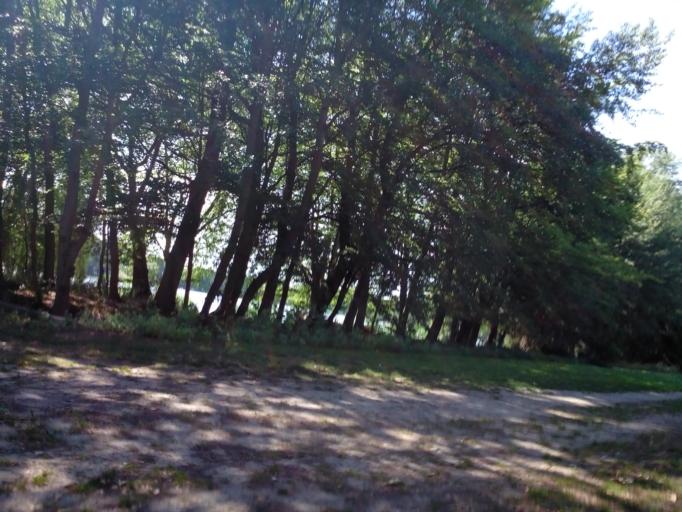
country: BE
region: Flanders
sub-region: Provincie Vlaams-Brabant
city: Leuven
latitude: 50.8950
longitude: 4.7271
